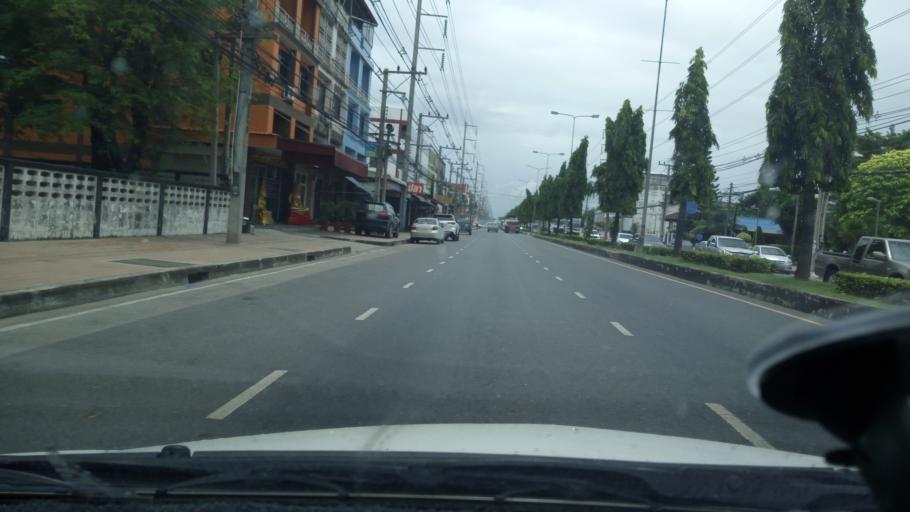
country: TH
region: Chon Buri
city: Phanat Nikhom
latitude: 13.4530
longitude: 101.1751
